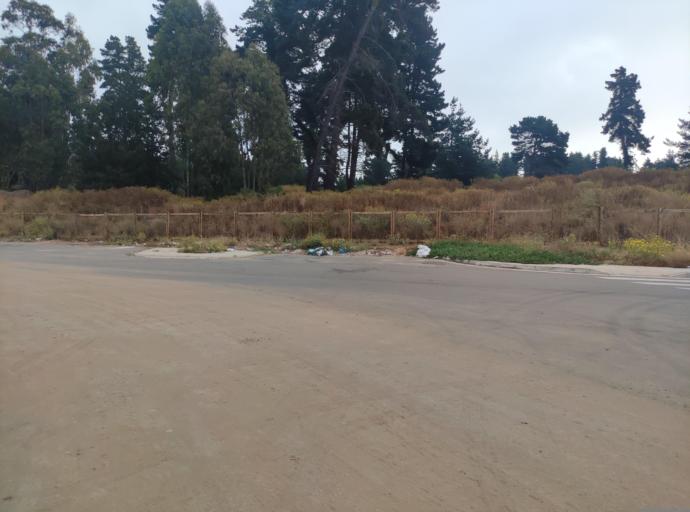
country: CL
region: Valparaiso
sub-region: Provincia de Valparaiso
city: Vina del Mar
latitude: -32.9442
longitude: -71.5166
